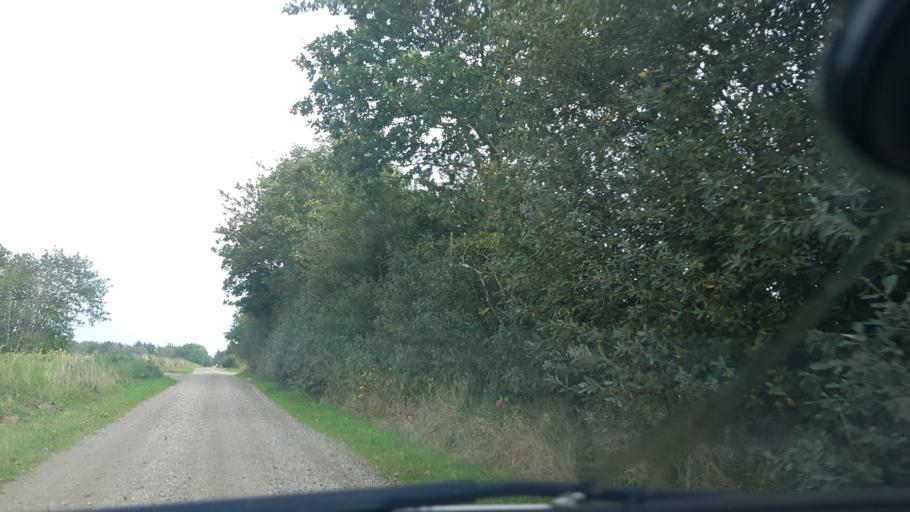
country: DK
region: South Denmark
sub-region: Vejen Kommune
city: Holsted
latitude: 55.4451
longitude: 8.9282
